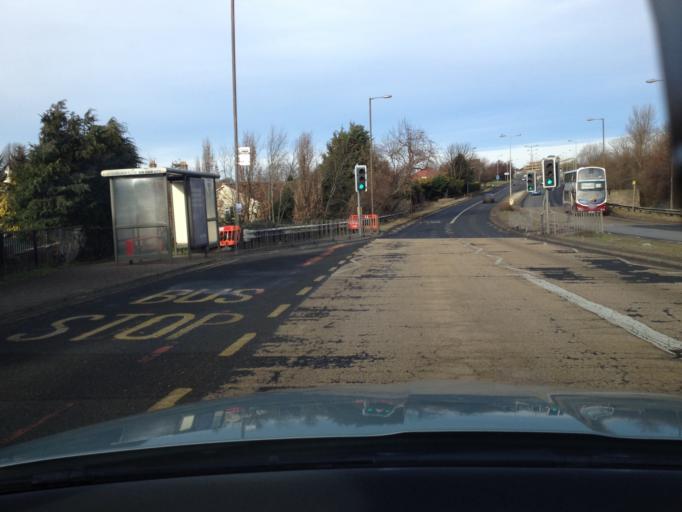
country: GB
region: Scotland
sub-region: Midlothian
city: Loanhead
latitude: 55.8938
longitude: -3.1617
